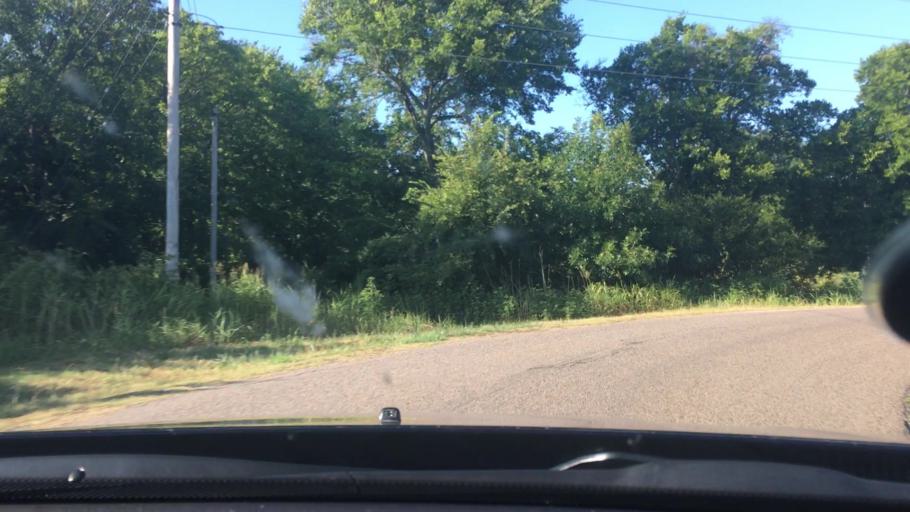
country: US
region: Oklahoma
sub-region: Murray County
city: Sulphur
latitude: 34.4043
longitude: -96.8199
